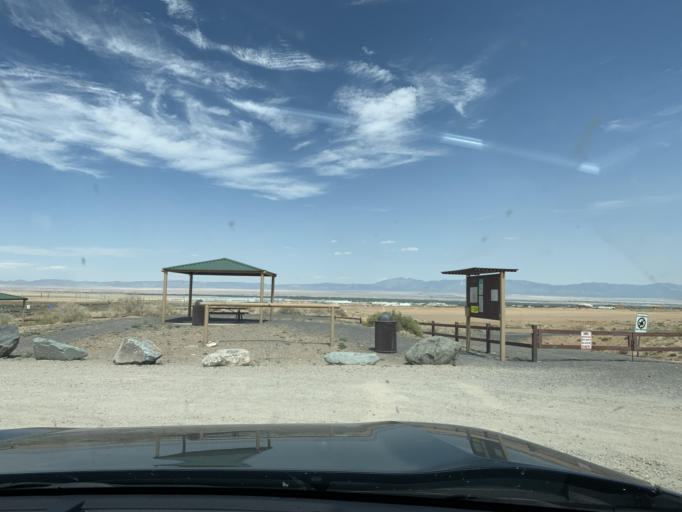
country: US
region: New Mexico
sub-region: Valencia County
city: Los Lunas
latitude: 34.8224
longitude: -106.8116
